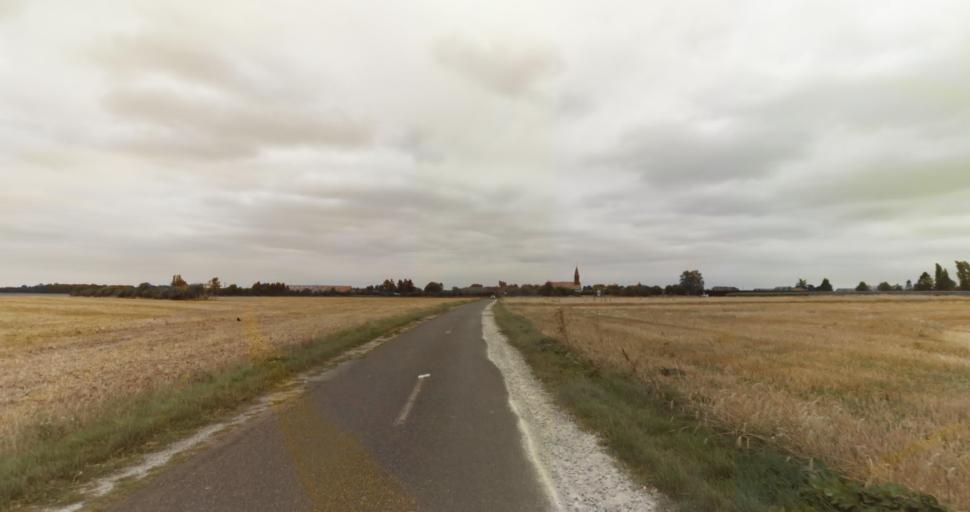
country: FR
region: Haute-Normandie
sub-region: Departement de l'Eure
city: La Couture-Boussey
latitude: 48.9122
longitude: 1.3432
